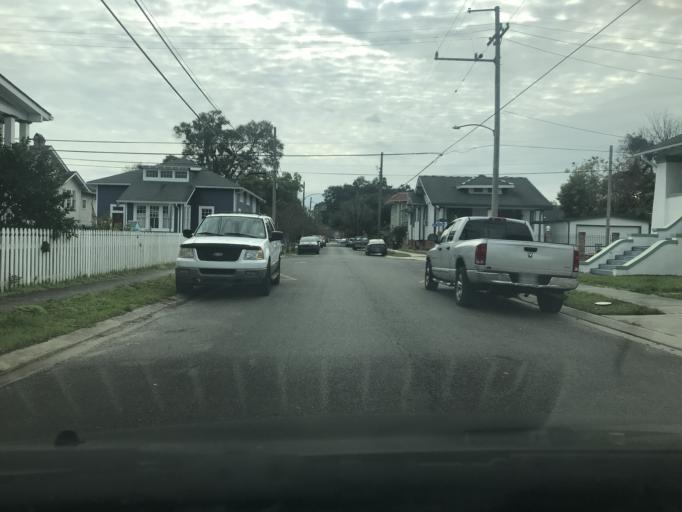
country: US
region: Louisiana
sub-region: Orleans Parish
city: New Orleans
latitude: 29.9504
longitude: -90.1044
